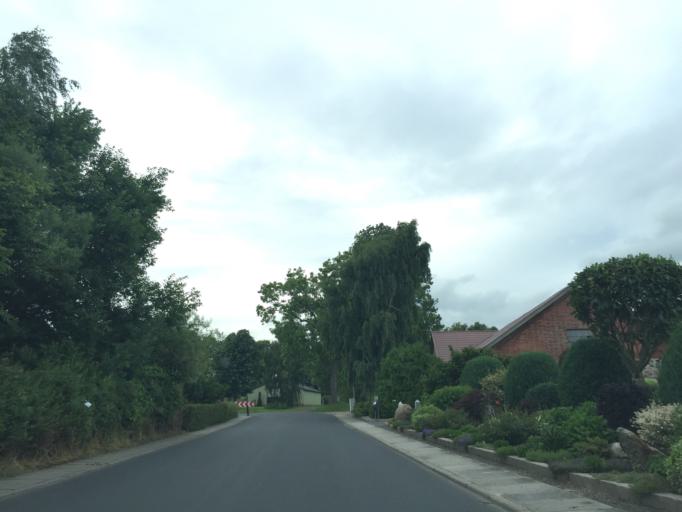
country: DK
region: Central Jutland
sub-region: Silkeborg Kommune
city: Silkeborg
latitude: 56.2242
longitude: 9.5644
